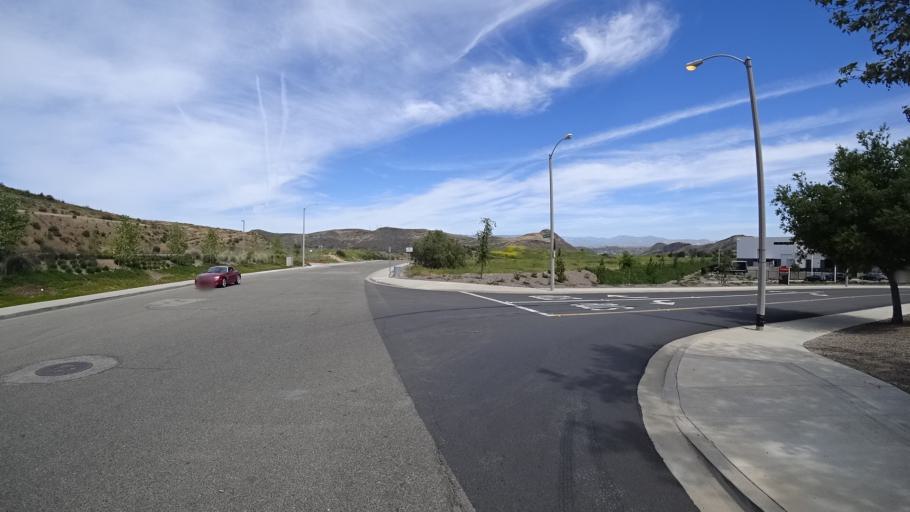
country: US
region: California
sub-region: Ventura County
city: Casa Conejo
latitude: 34.1999
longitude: -118.9340
